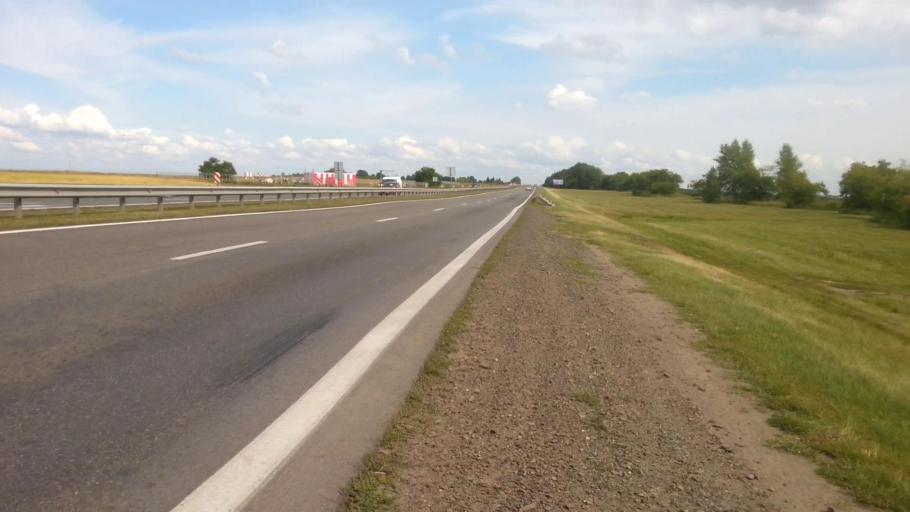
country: RU
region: Altai Krai
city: Nauchnyy Gorodok
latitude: 53.3564
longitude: 83.5104
